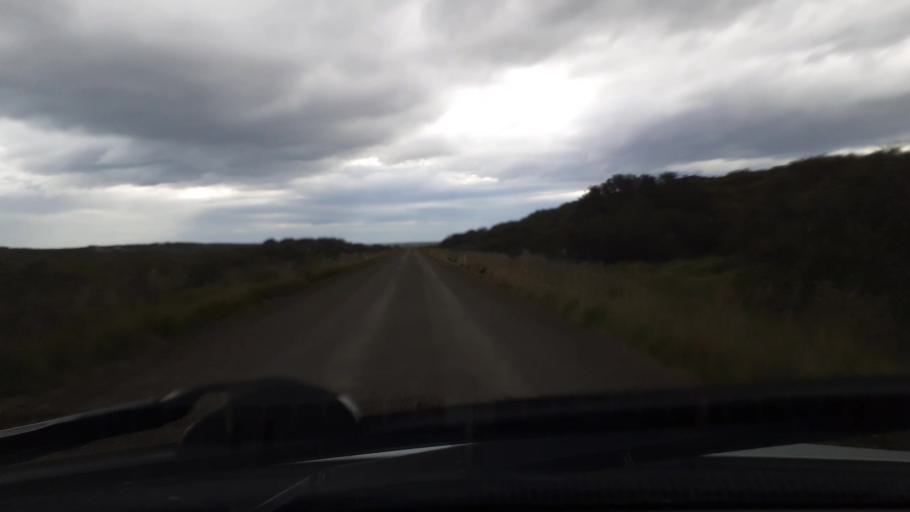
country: IS
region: West
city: Borgarnes
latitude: 64.6039
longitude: -21.9686
